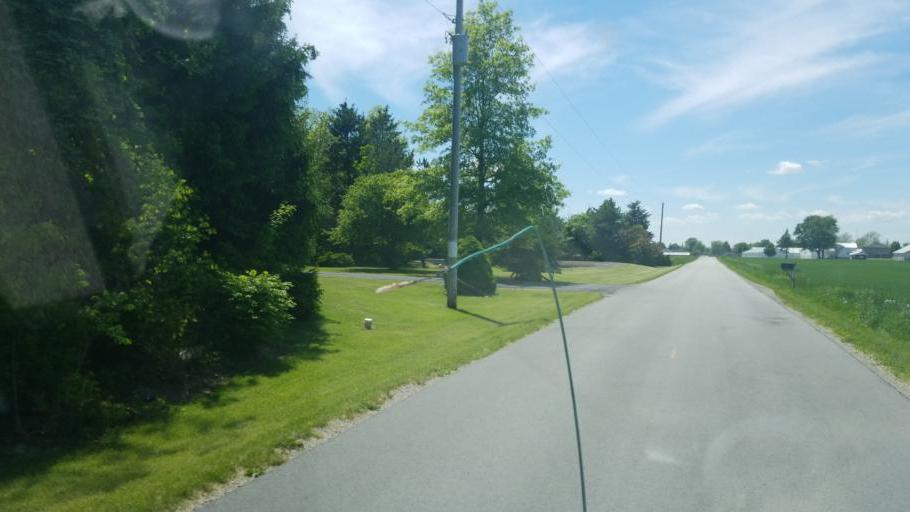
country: US
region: Ohio
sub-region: Huron County
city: Willard
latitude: 41.0663
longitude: -82.8722
